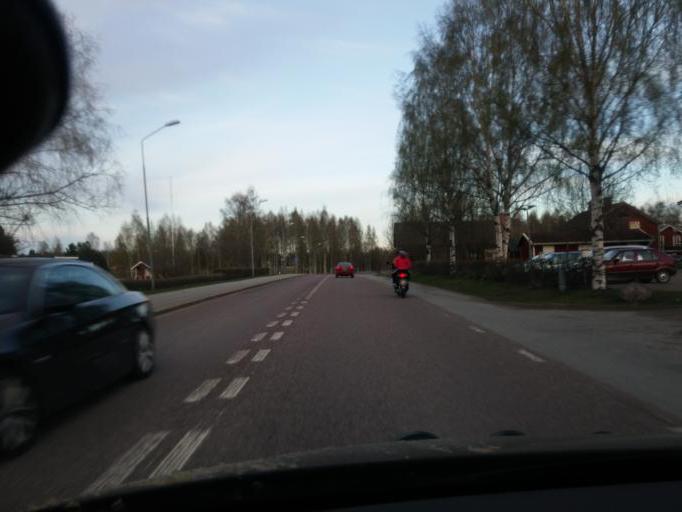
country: SE
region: Gaevleborg
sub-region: Ljusdals Kommun
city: Ljusdal
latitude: 61.8361
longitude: 16.0640
